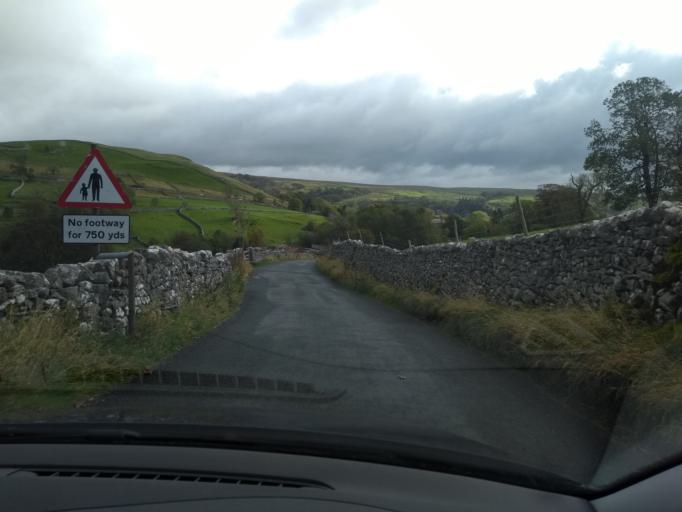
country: GB
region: England
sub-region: North Yorkshire
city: Gargrave
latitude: 54.0660
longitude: -2.1585
